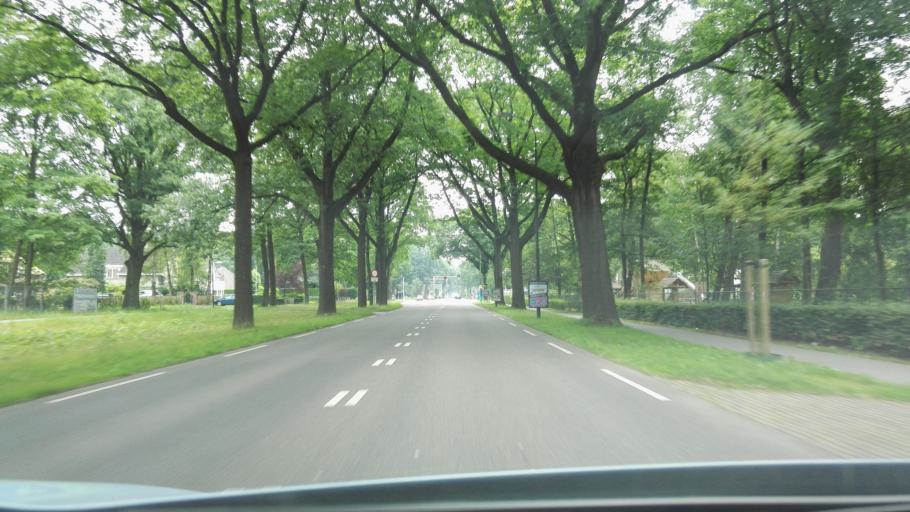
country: NL
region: Gelderland
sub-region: Gemeente Apeldoorn
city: Beekbergen
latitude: 52.1827
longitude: 5.9621
